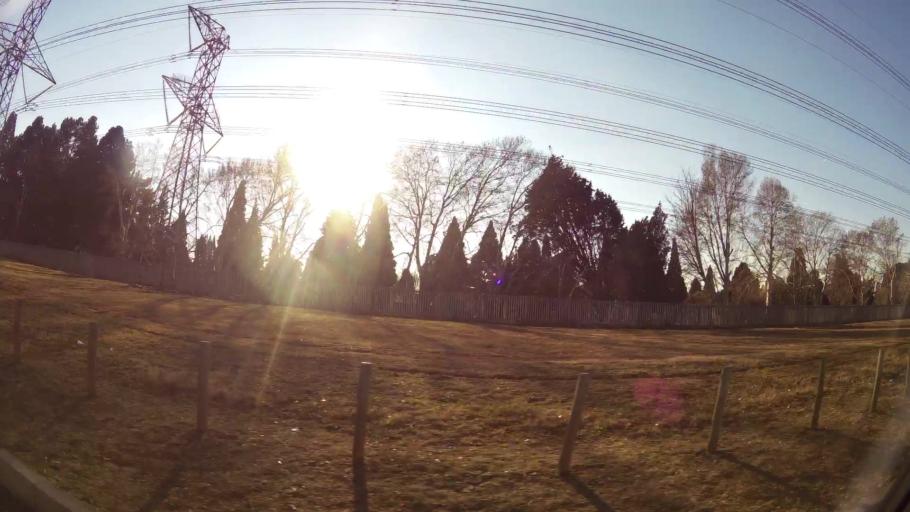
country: ZA
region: Gauteng
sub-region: Ekurhuleni Metropolitan Municipality
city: Germiston
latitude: -26.1959
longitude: 28.1417
